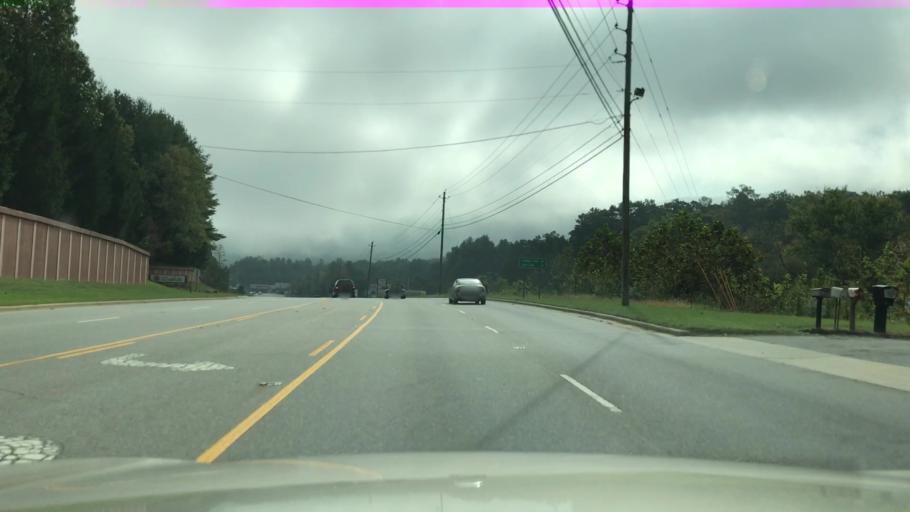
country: US
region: North Carolina
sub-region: Buncombe County
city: Biltmore Forest
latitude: 35.5544
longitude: -82.4814
